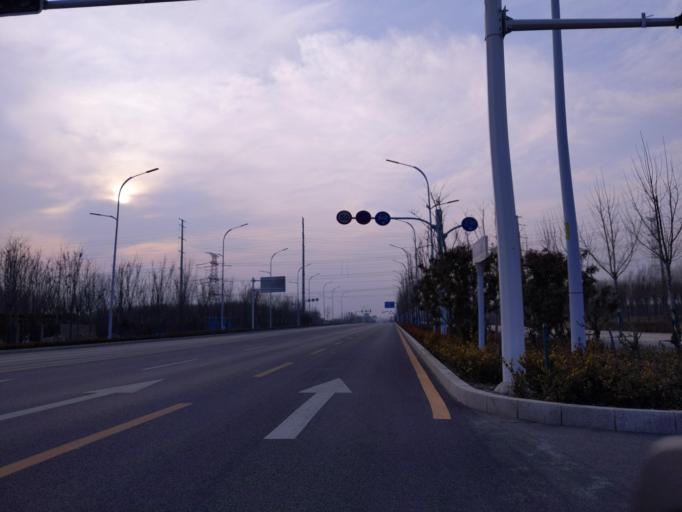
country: CN
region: Henan Sheng
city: Puyang
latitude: 35.8188
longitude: 115.0001
